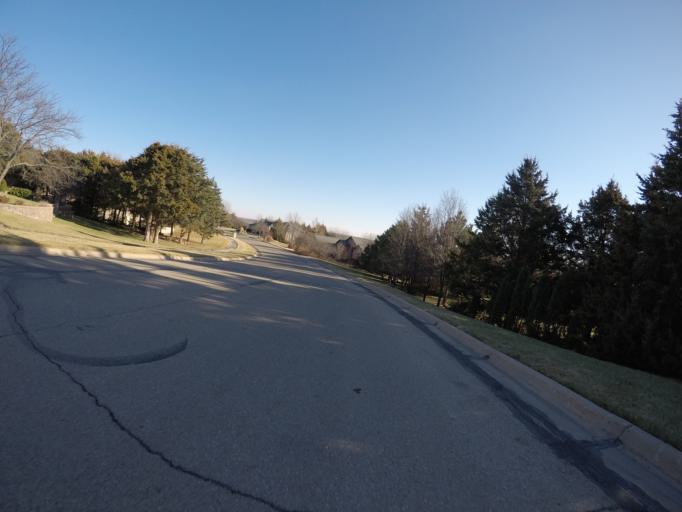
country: US
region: Kansas
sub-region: Riley County
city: Manhattan
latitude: 39.1959
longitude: -96.6378
